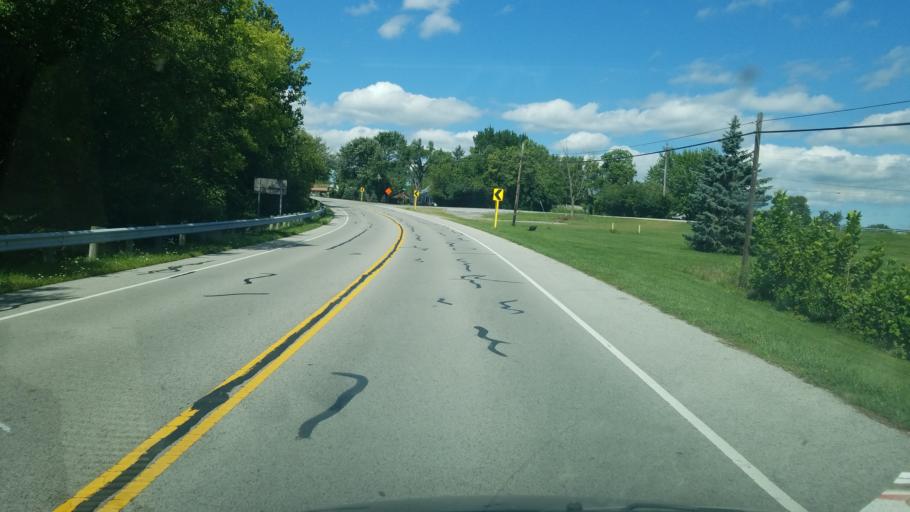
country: US
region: Ohio
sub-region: Wood County
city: Weston
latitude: 41.4179
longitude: -83.8682
